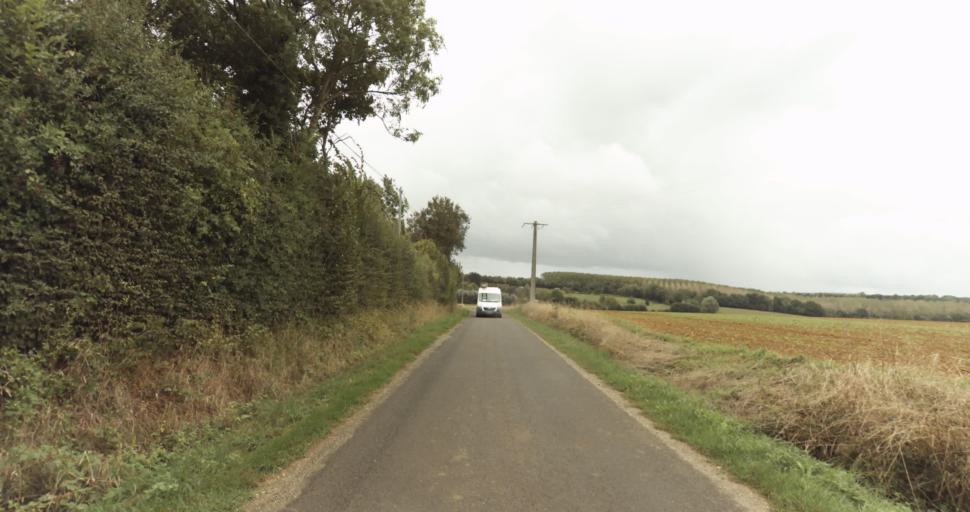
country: FR
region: Lower Normandy
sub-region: Departement de l'Orne
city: Sainte-Gauburge-Sainte-Colombe
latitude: 48.7231
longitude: 0.3785
